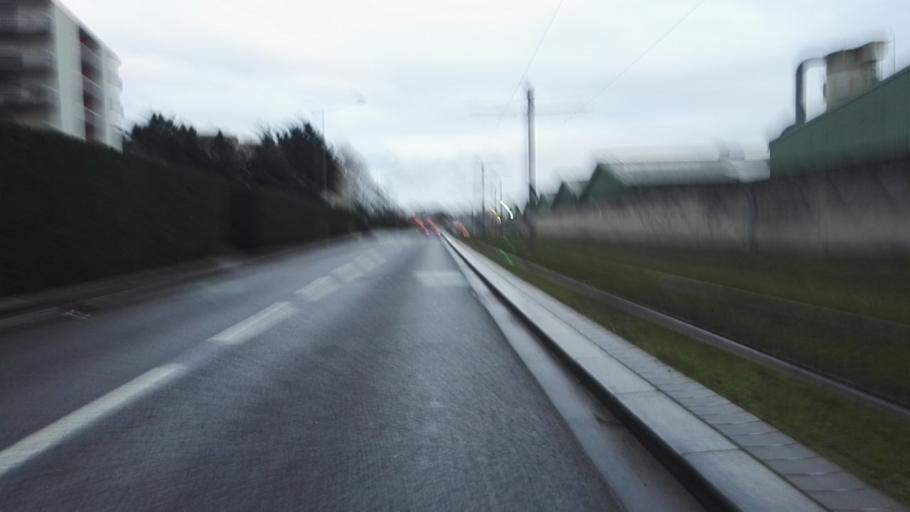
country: FR
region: Aquitaine
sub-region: Departement de la Gironde
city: Merignac
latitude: 44.8302
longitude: -0.6322
